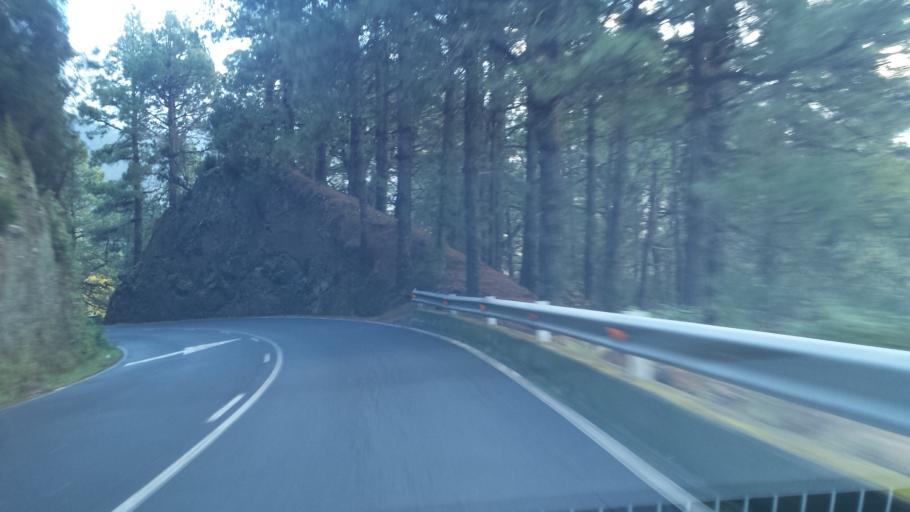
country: ES
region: Canary Islands
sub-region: Provincia de Santa Cruz de Tenerife
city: Brena Baja
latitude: 28.6475
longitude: -17.8328
